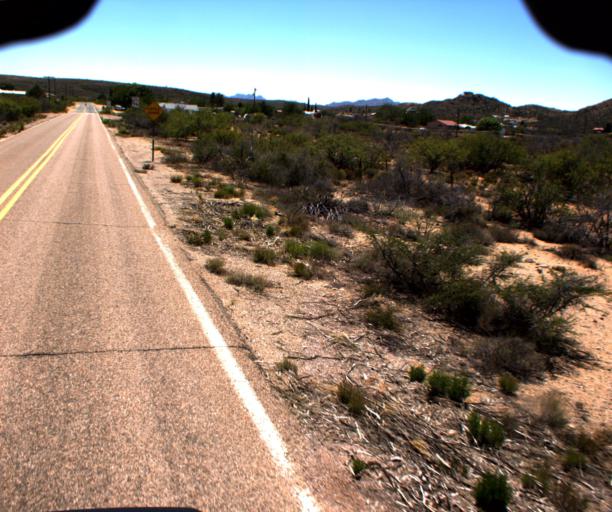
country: US
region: Arizona
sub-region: Yavapai County
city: Congress
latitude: 34.4247
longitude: -112.9161
